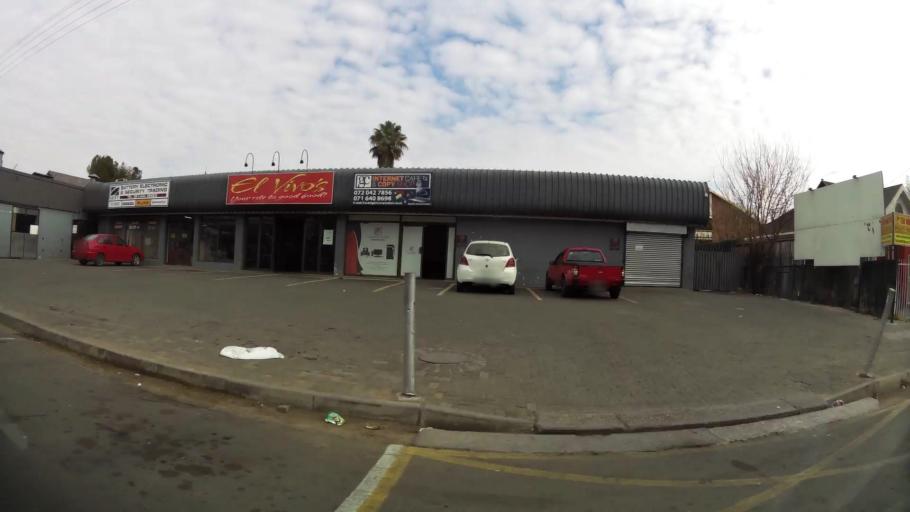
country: ZA
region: Orange Free State
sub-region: Mangaung Metropolitan Municipality
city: Bloemfontein
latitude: -29.1202
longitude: 26.2039
